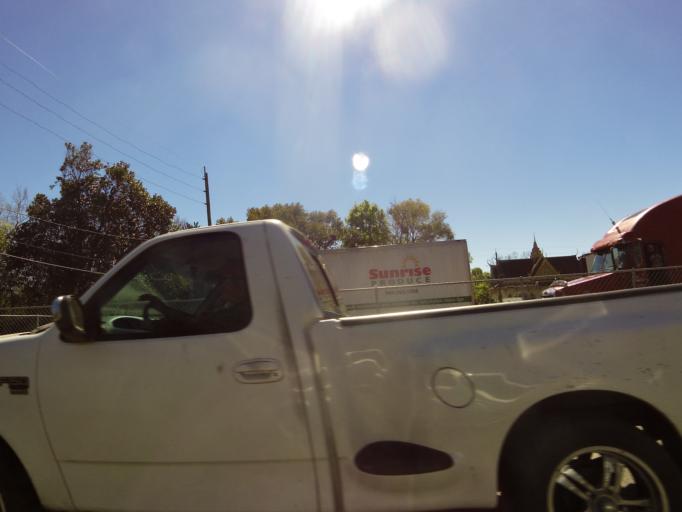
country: US
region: Florida
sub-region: Duval County
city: Jacksonville
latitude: 30.3246
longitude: -81.7174
